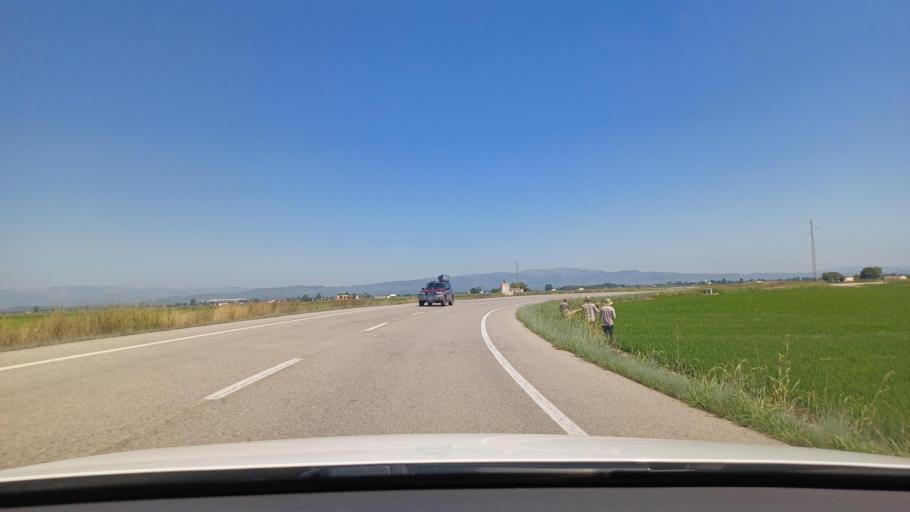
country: ES
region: Catalonia
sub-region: Provincia de Tarragona
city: Deltebre
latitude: 40.6908
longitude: 0.6833
